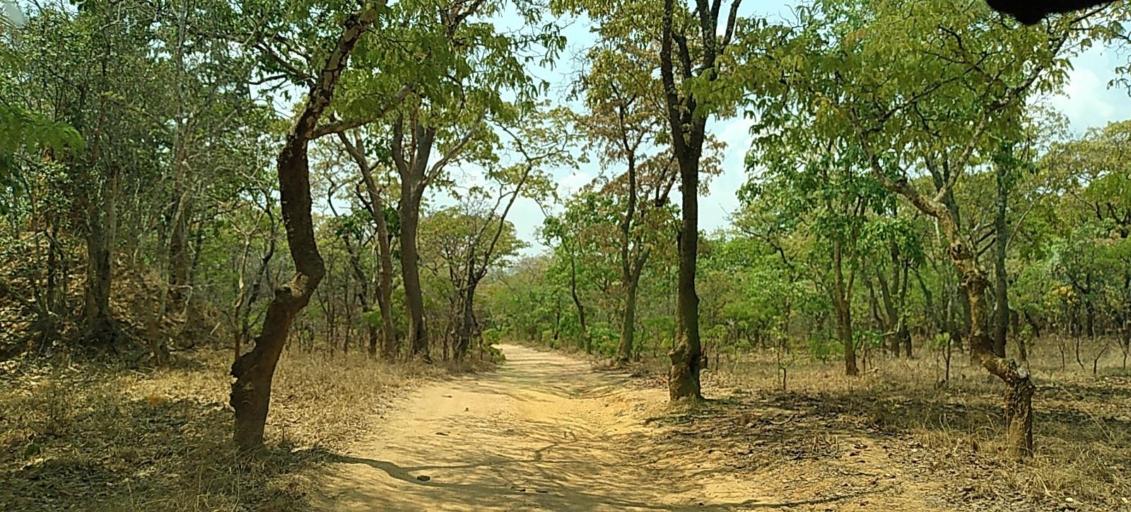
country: ZM
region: North-Western
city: Kabompo
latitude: -13.6497
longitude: 24.3752
